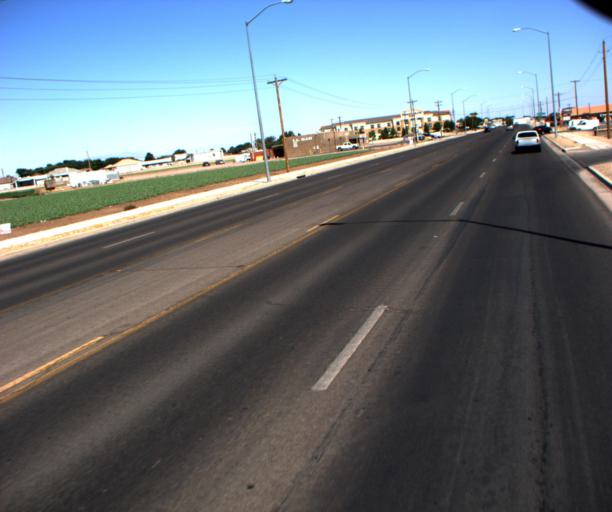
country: US
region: Arizona
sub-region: Graham County
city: Thatcher
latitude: 32.8447
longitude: -109.7435
